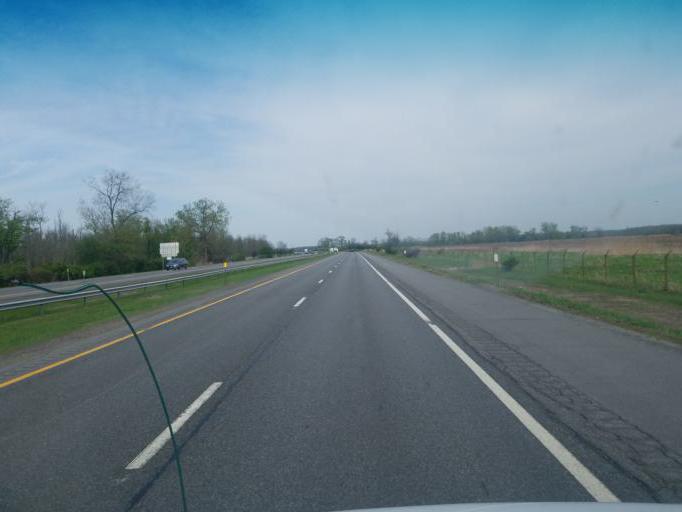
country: US
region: New York
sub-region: Seneca County
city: Bridgeport
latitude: 42.9839
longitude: -76.7798
